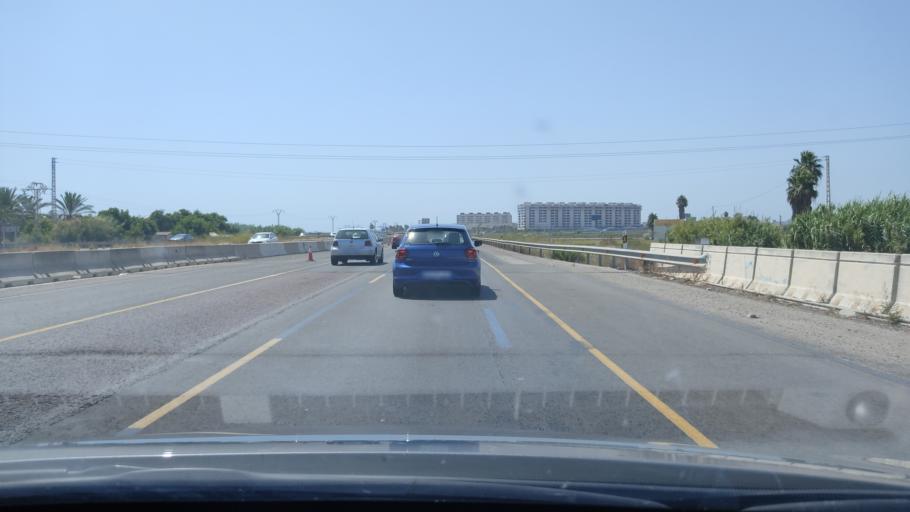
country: ES
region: Valencia
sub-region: Provincia de Valencia
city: Alboraya
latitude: 39.5024
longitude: -0.3261
